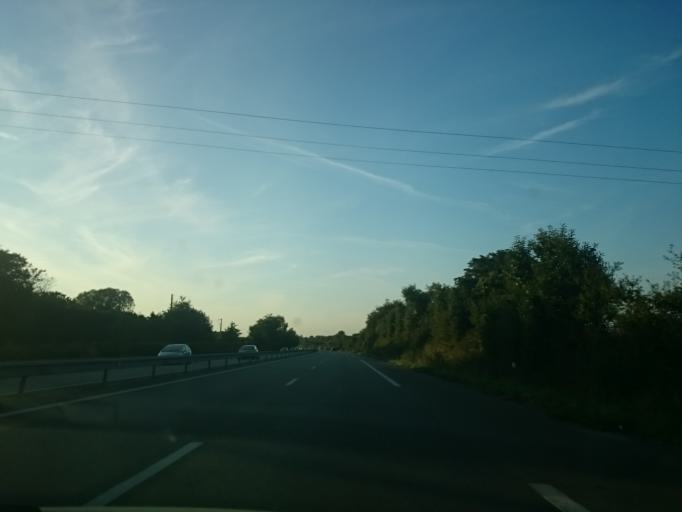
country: FR
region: Brittany
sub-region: Departement du Morbihan
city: Brech
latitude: 47.6981
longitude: -3.0385
